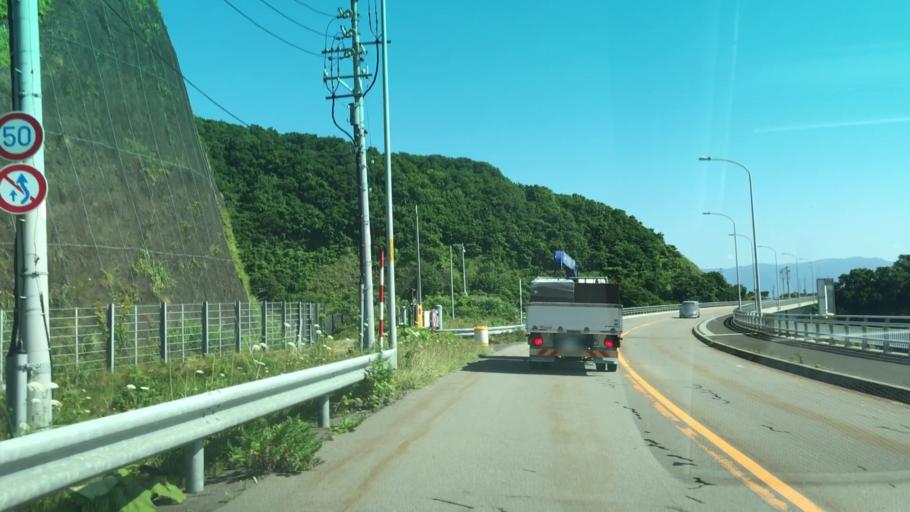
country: JP
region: Hokkaido
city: Iwanai
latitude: 43.1269
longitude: 140.4425
